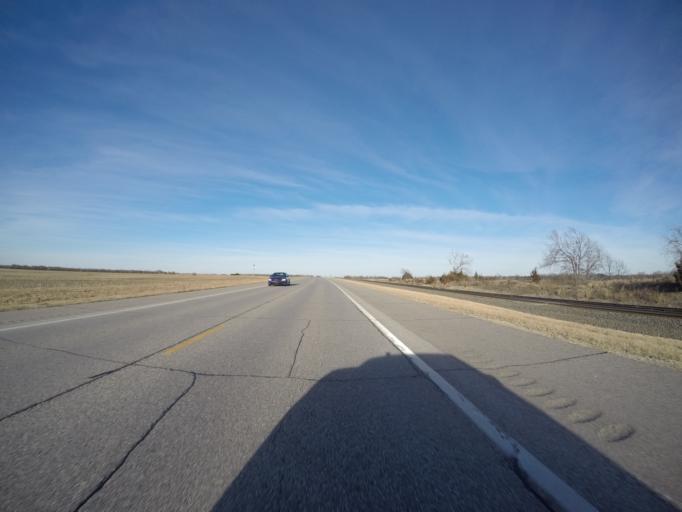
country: US
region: Kansas
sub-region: Harvey County
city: North Newton
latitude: 38.1244
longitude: -97.2481
